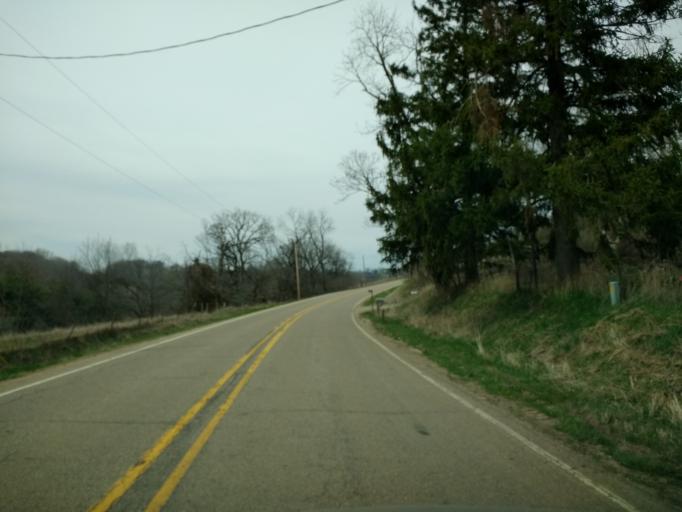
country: US
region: Iowa
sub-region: Monona County
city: Mapleton
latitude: 42.2342
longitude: -95.9441
